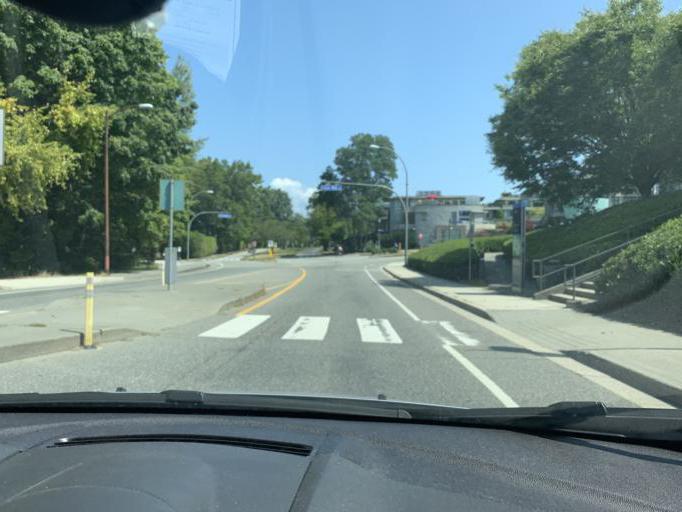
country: CA
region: British Columbia
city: West End
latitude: 49.2707
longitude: -123.2548
